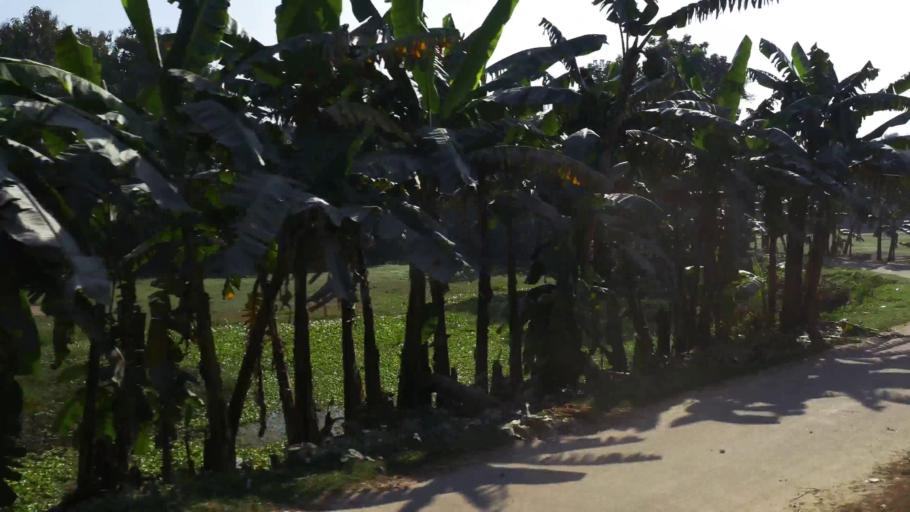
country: BD
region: Dhaka
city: Muktagacha
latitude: 24.8024
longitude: 90.3069
